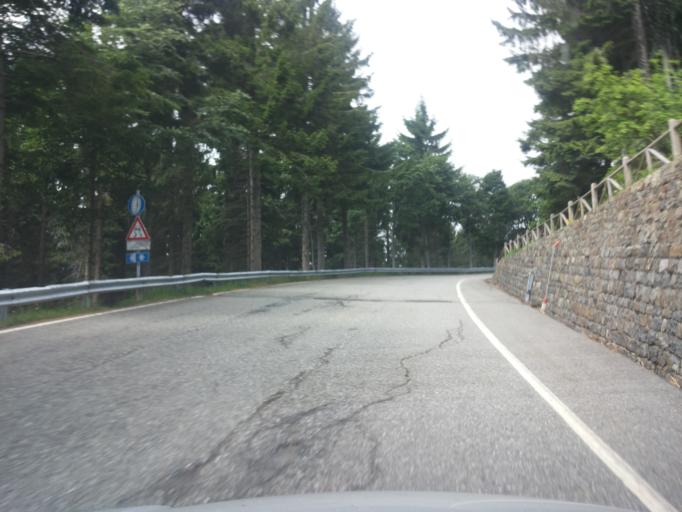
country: IT
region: Piedmont
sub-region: Provincia di Biella
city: Camandona
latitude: 45.6618
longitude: 8.0880
